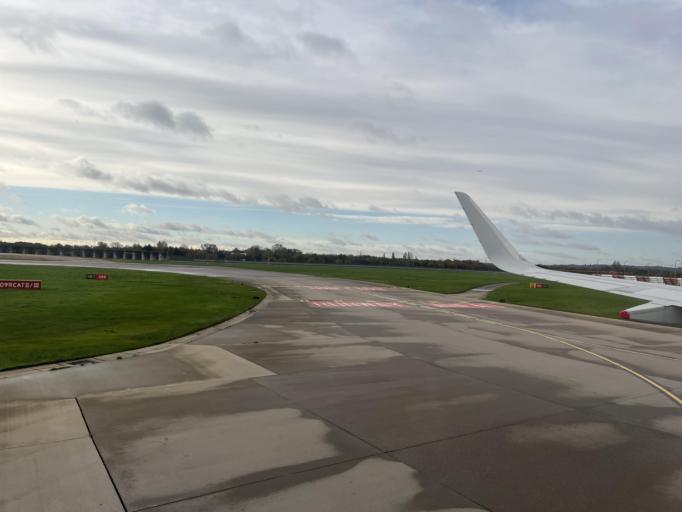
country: GB
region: England
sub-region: Buckinghamshire
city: Iver
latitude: 51.4665
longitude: -0.4870
